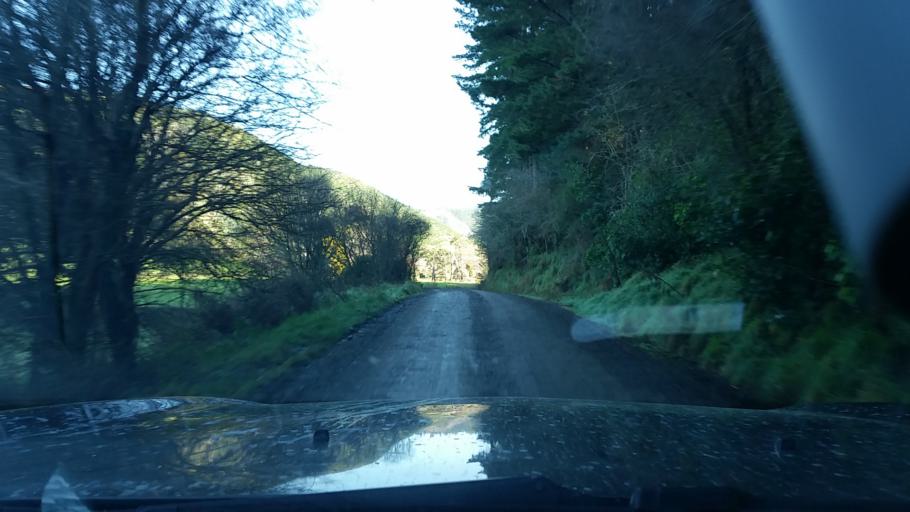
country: NZ
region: Marlborough
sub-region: Marlborough District
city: Blenheim
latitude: -41.4633
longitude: 173.7947
